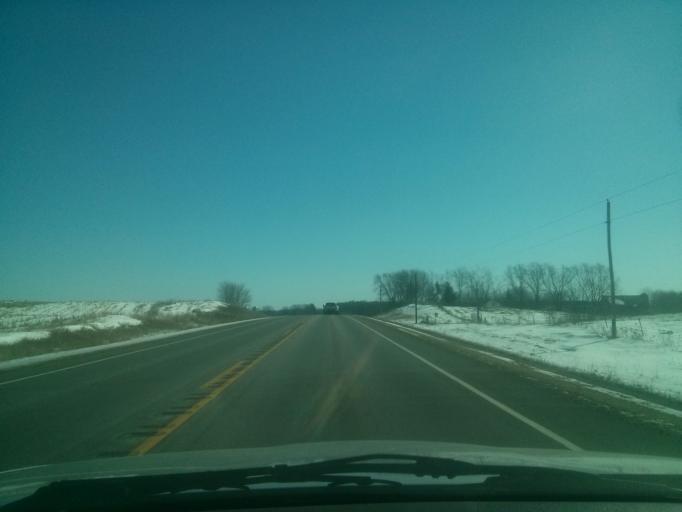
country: US
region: Wisconsin
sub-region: Polk County
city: Clear Lake
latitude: 45.1364
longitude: -92.2982
